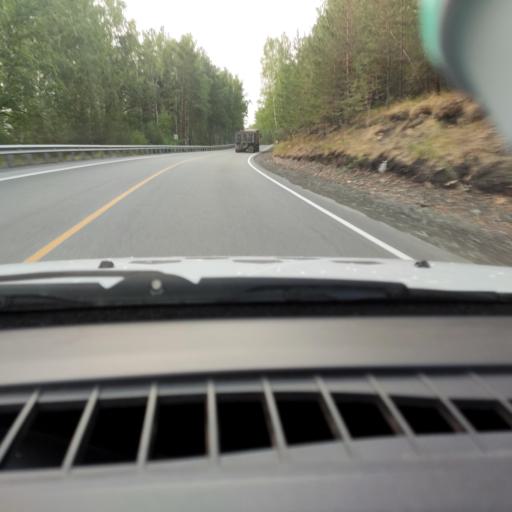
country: RU
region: Chelyabinsk
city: Turgoyak
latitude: 55.2448
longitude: 60.1975
